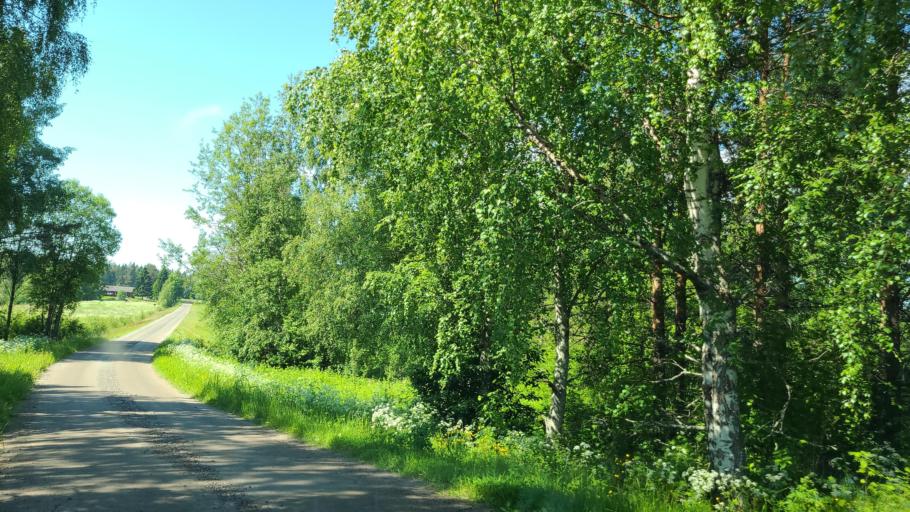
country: SE
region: Vaesterbotten
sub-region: Robertsfors Kommun
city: Robertsfors
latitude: 64.0883
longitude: 20.8485
